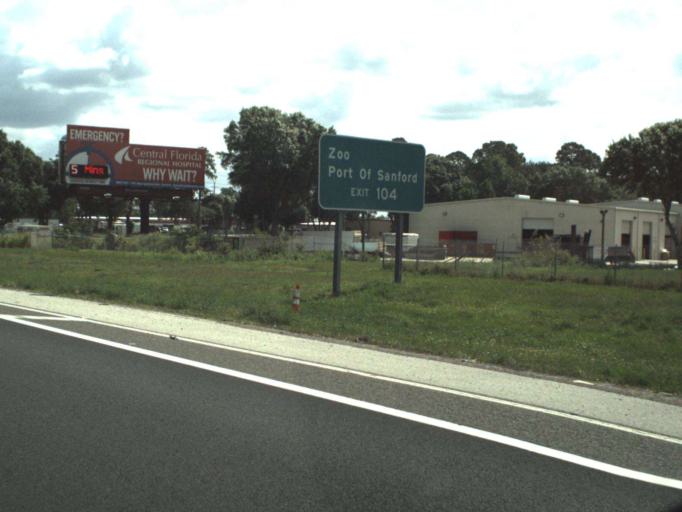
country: US
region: Florida
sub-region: Seminole County
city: Lake Mary
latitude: 28.8193
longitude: -81.3338
